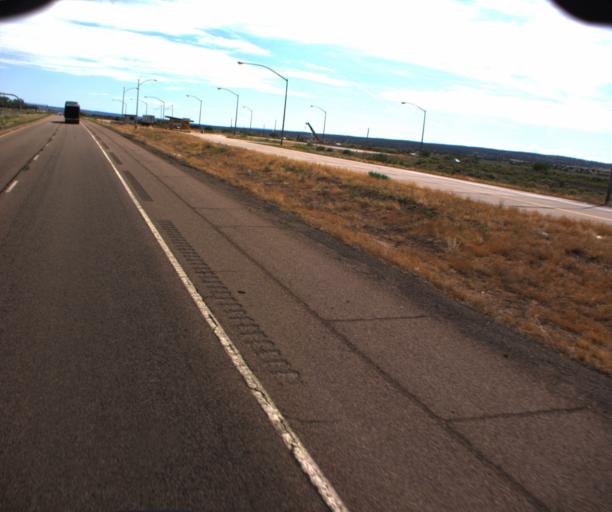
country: US
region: Arizona
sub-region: Apache County
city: Houck
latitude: 35.2222
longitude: -109.3227
